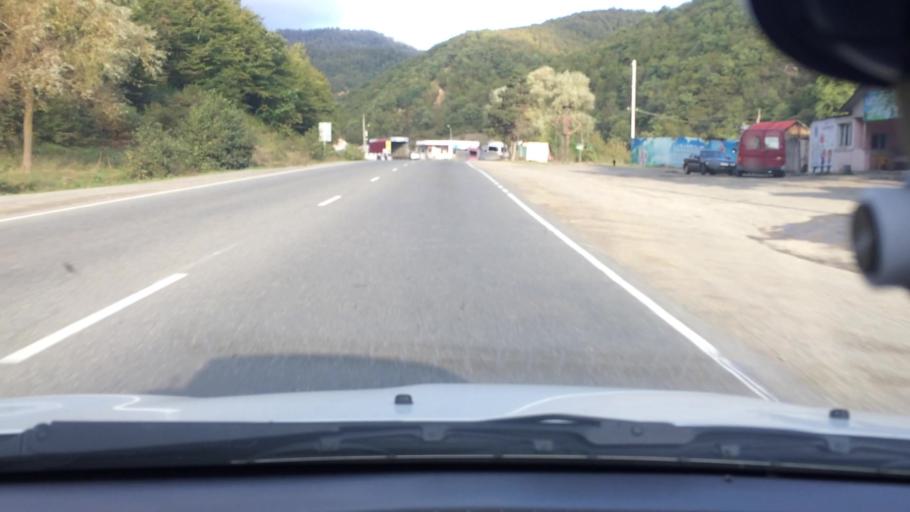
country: GE
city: Surami
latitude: 42.0395
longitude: 43.5121
